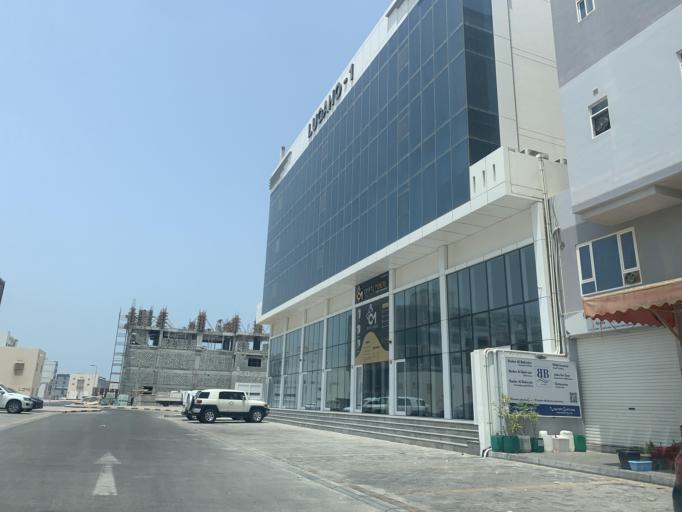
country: BH
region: Muharraq
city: Al Hadd
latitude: 26.2556
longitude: 50.6654
